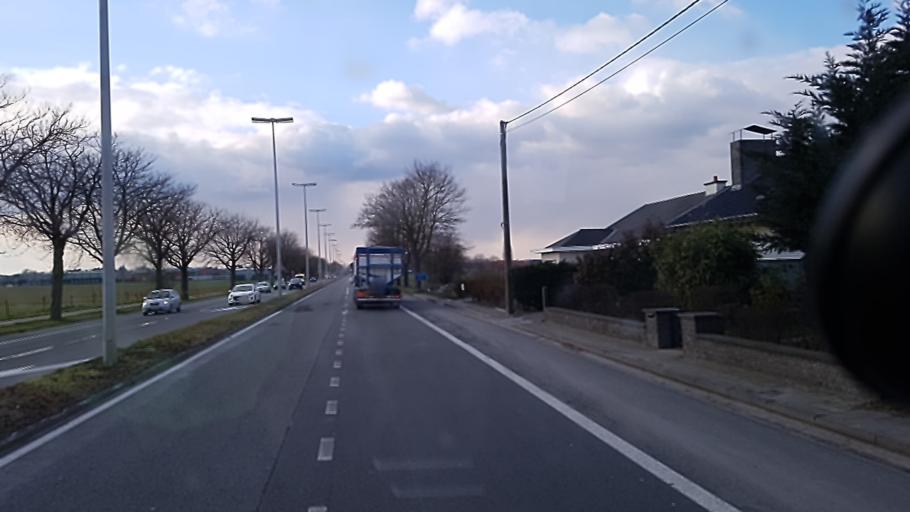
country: BE
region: Wallonia
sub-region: Province du Hainaut
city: Estaimpuis
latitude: 50.7306
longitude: 3.2905
